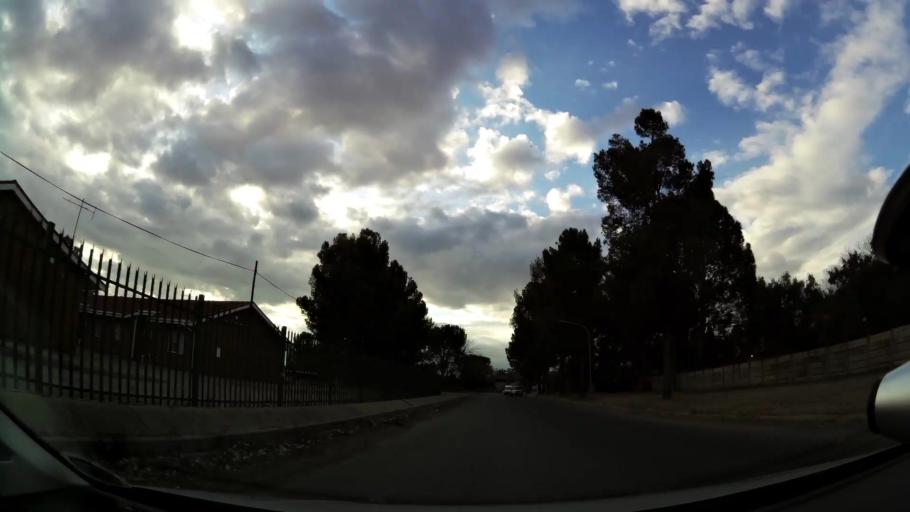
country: ZA
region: Orange Free State
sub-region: Lejweleputswa District Municipality
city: Welkom
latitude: -27.9963
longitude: 26.7183
